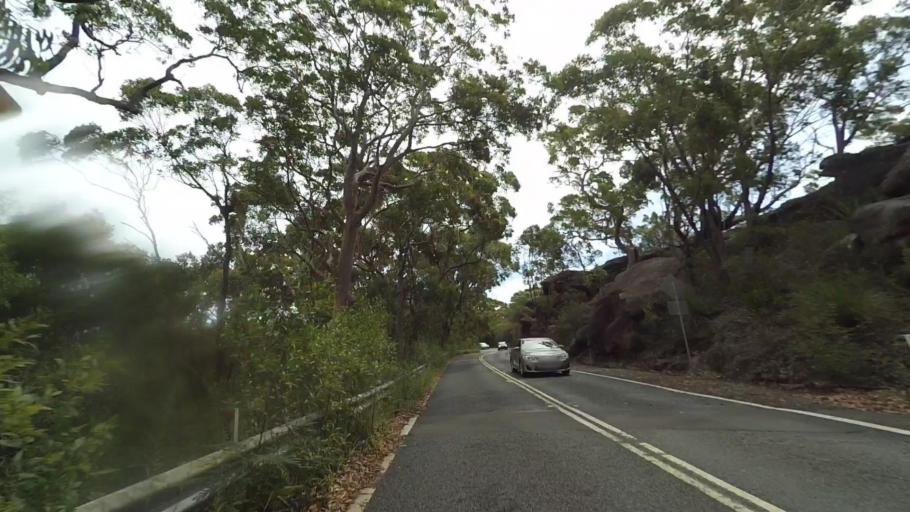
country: AU
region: New South Wales
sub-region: Sutherland Shire
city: Heathcote
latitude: -34.1148
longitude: 151.0643
